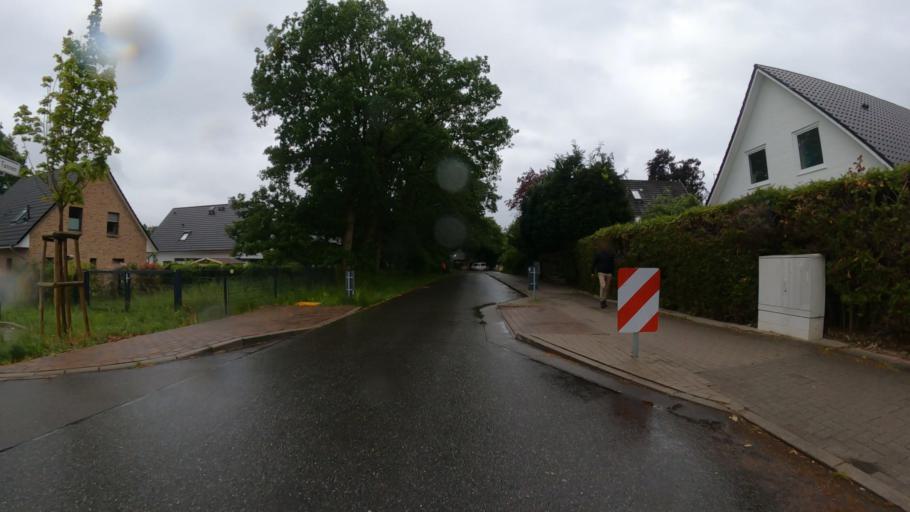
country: DE
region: Schleswig-Holstein
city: Norderstedt
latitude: 53.6994
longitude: 10.0036
